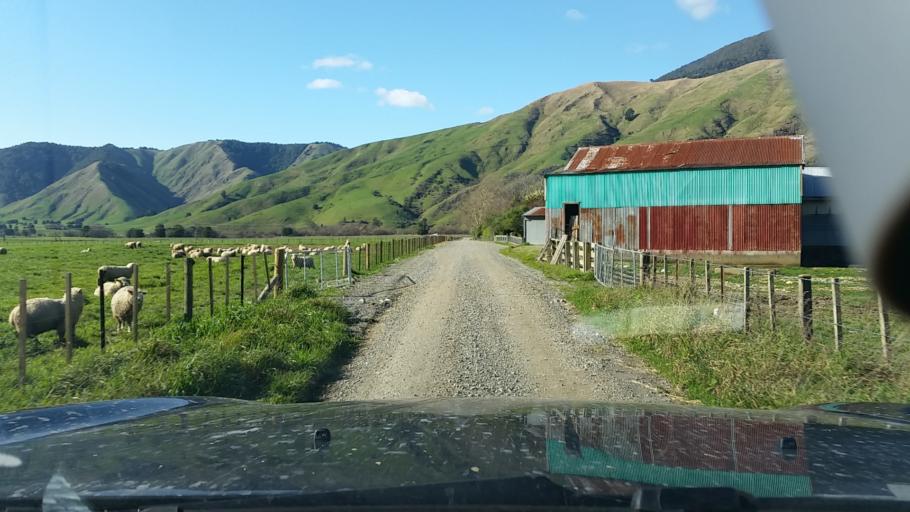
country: NZ
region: Marlborough
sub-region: Marlborough District
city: Picton
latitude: -41.3189
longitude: 173.7604
